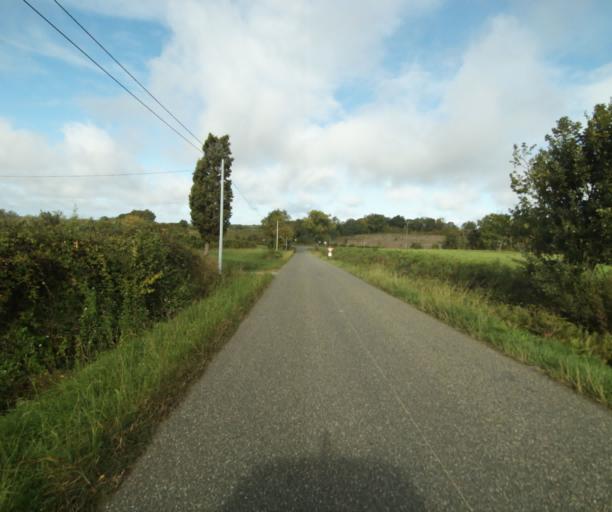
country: FR
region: Midi-Pyrenees
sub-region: Departement du Gers
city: Cazaubon
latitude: 43.8641
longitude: -0.0639
